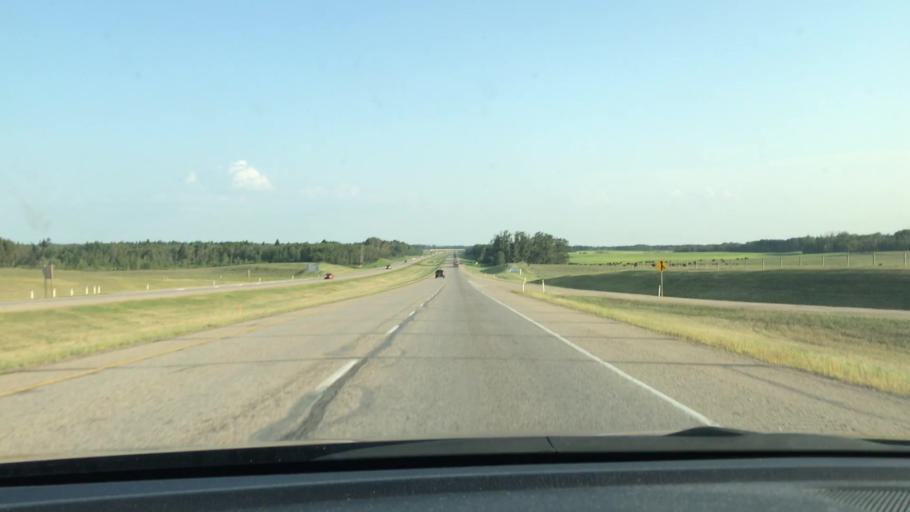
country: CA
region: Alberta
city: Ponoka
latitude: 52.5780
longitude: -113.6632
